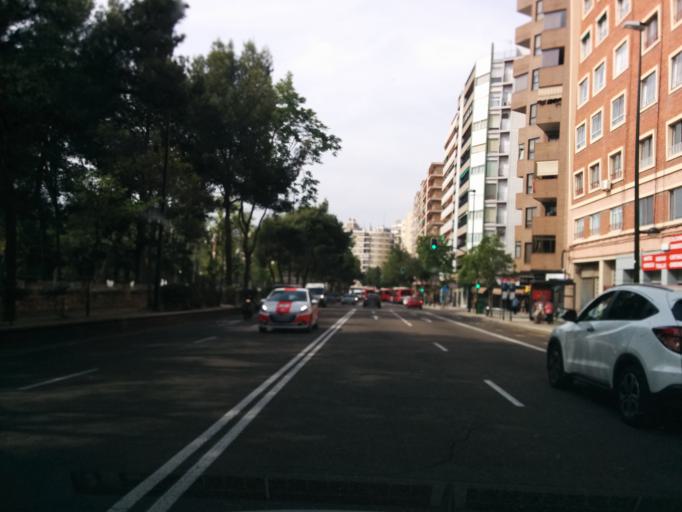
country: ES
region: Aragon
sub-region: Provincia de Zaragoza
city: Zaragoza
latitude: 41.6357
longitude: -0.8847
